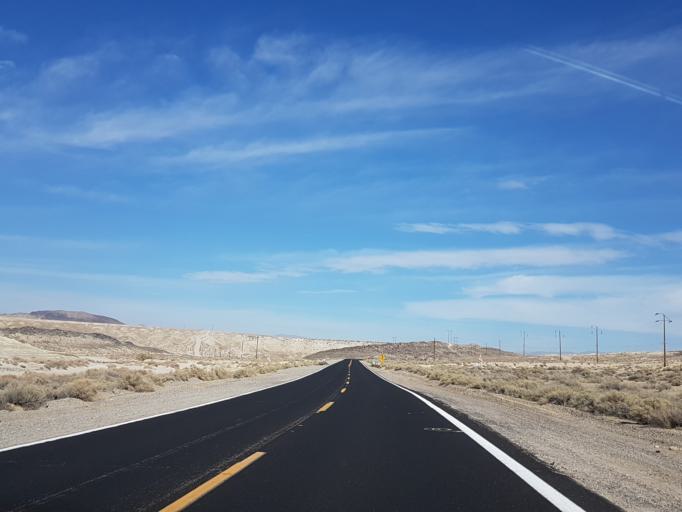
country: US
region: California
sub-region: San Bernardino County
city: Searles Valley
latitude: 35.6518
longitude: -117.4669
